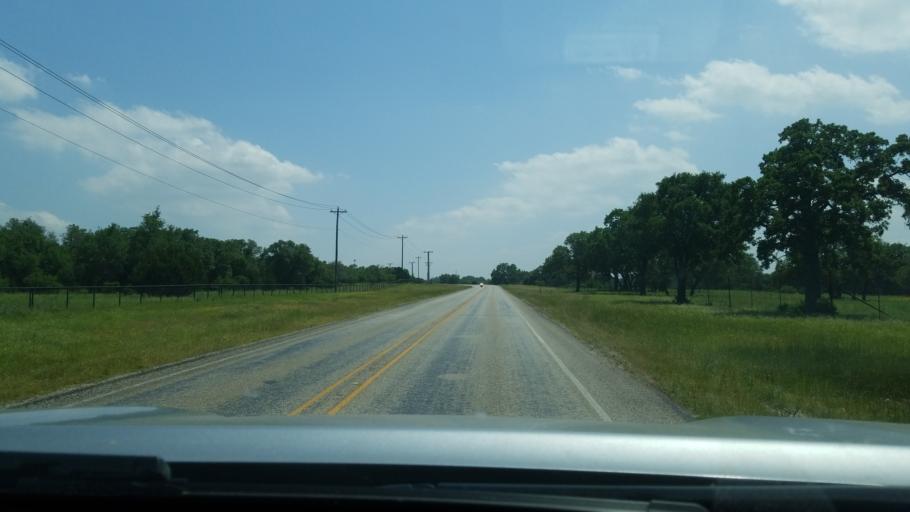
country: US
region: Texas
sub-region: Bexar County
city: Fair Oaks Ranch
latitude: 29.8807
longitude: -98.5579
